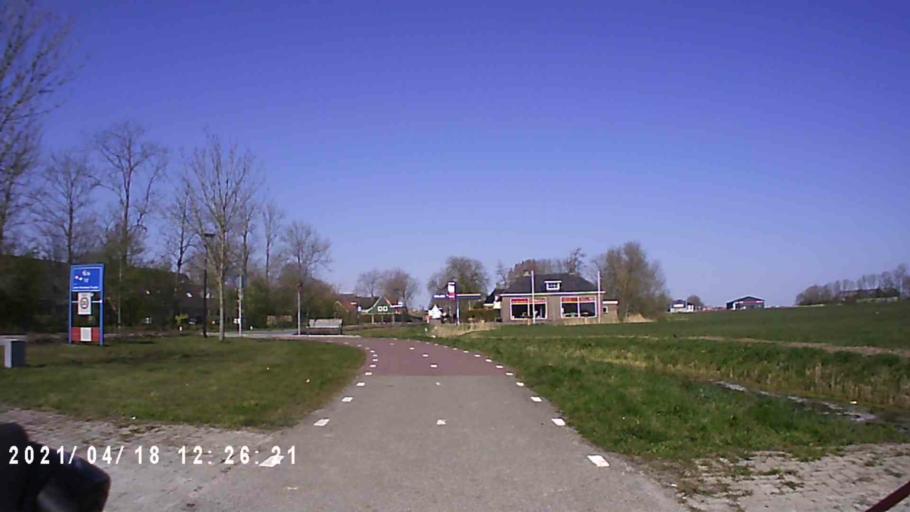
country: NL
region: Friesland
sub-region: Gemeente Dongeradeel
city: Anjum
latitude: 53.3296
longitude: 6.1058
